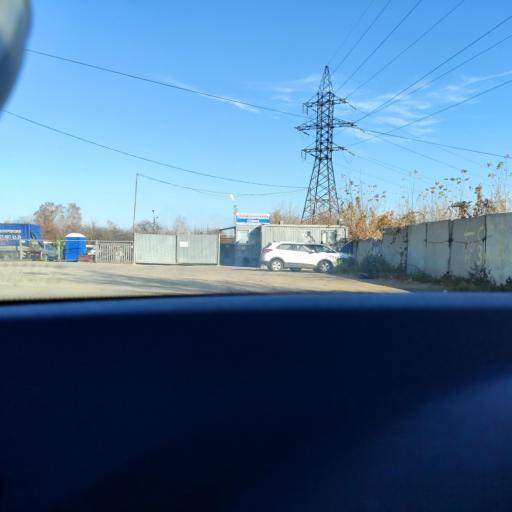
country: RU
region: Samara
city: Petra-Dubrava
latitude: 53.2621
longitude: 50.2910
